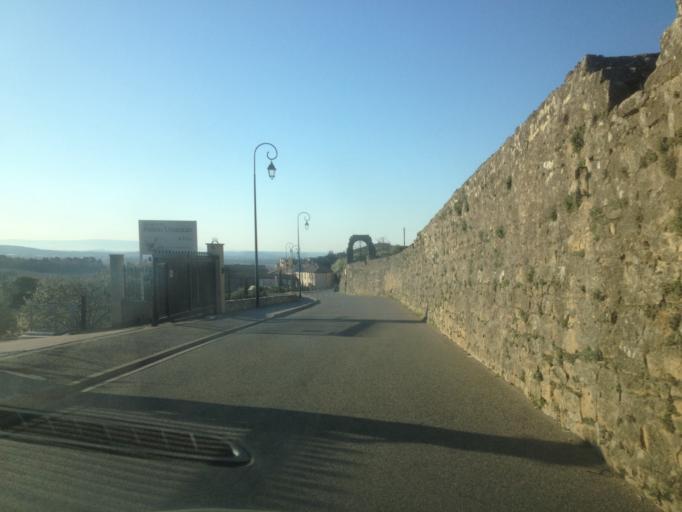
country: FR
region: Provence-Alpes-Cote d'Azur
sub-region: Departement du Vaucluse
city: Chateauneuf-du-Pape
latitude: 44.0599
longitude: 4.8295
